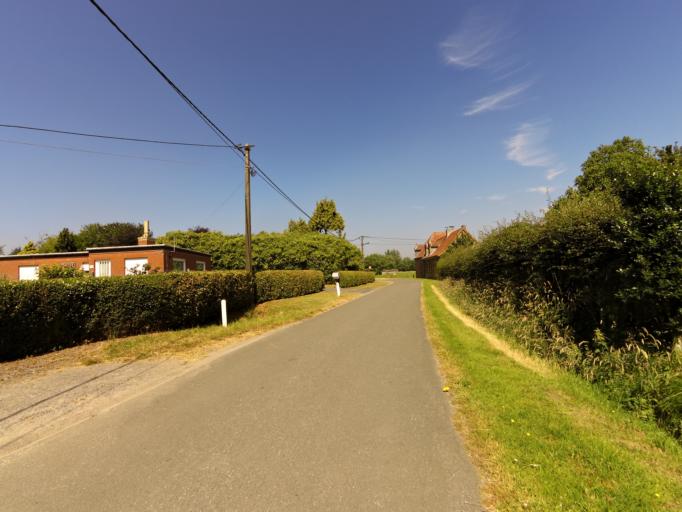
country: BE
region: Flanders
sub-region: Provincie West-Vlaanderen
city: Zedelgem
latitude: 51.1516
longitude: 3.1375
